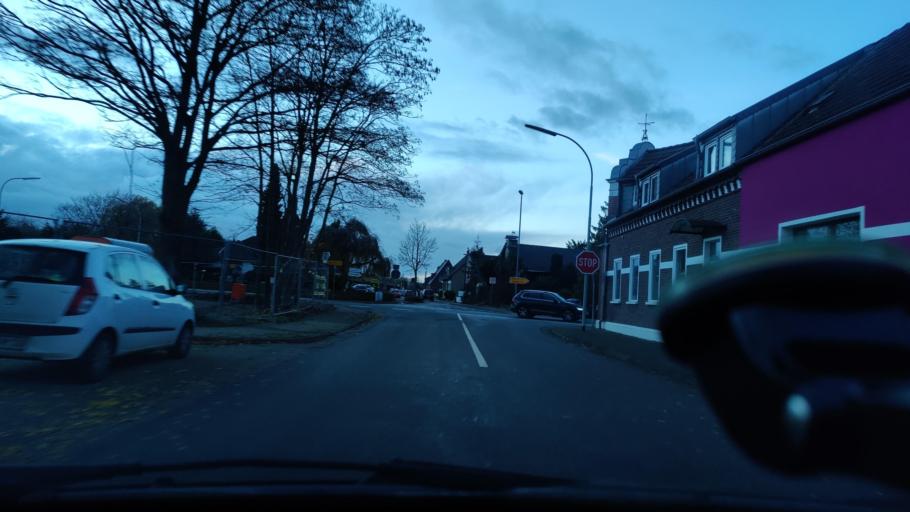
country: DE
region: North Rhine-Westphalia
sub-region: Regierungsbezirk Dusseldorf
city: Kevelaer
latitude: 51.5986
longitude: 6.2819
